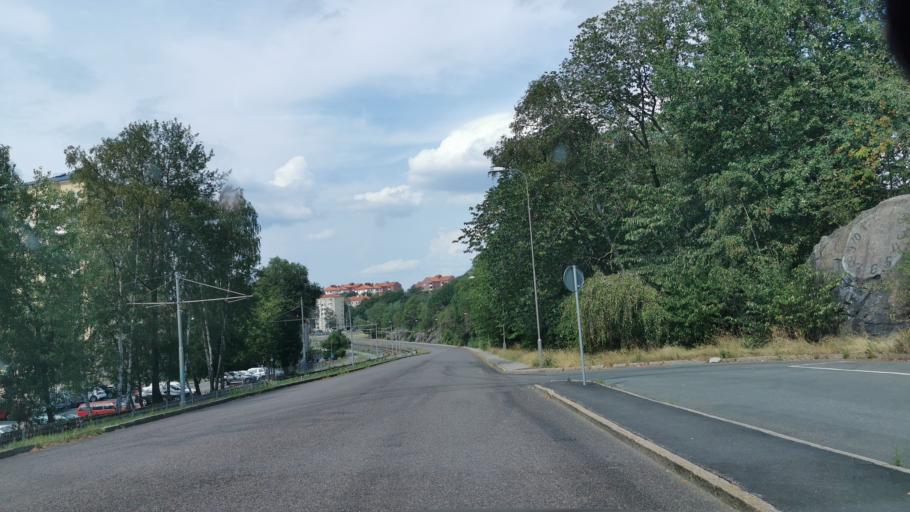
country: SE
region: Vaestra Goetaland
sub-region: Goteborg
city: Goeteborg
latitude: 57.6855
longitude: 11.9718
